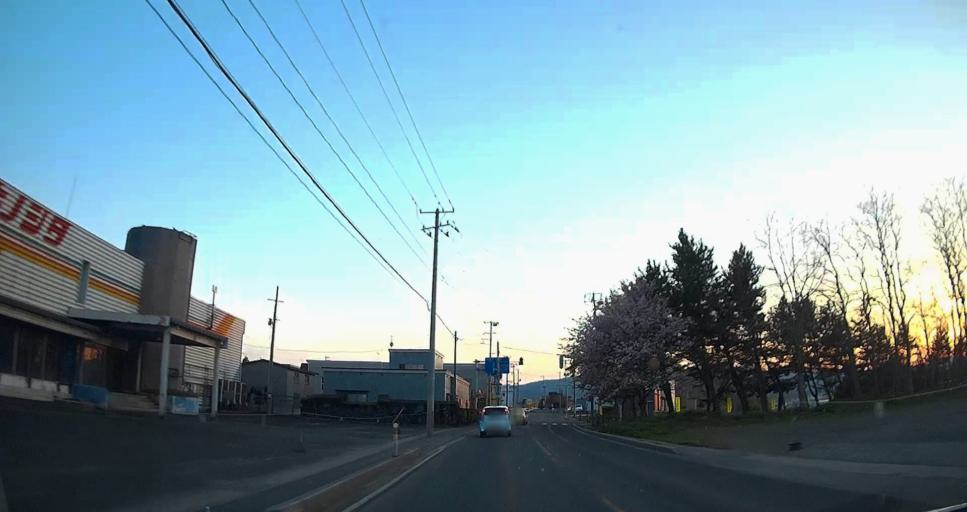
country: JP
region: Aomori
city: Misawa
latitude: 40.8731
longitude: 141.1354
